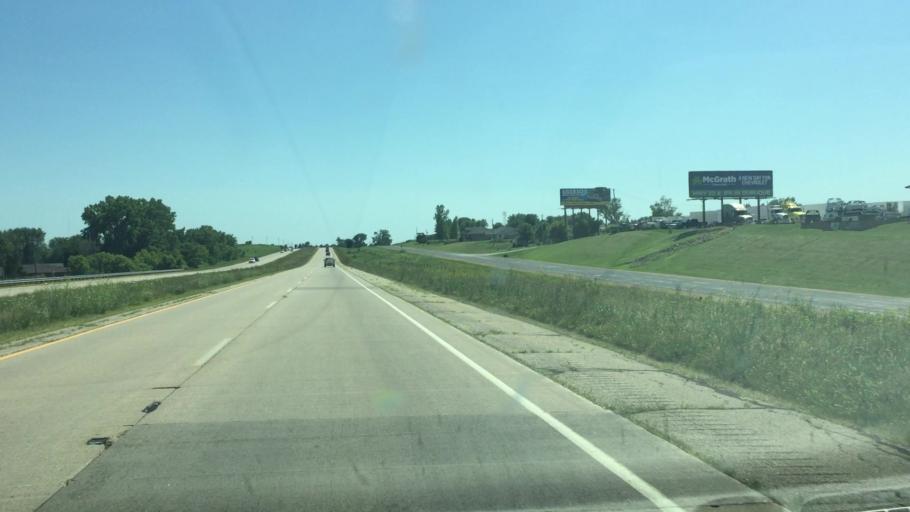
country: US
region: Wisconsin
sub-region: Grant County
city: Dickeyville
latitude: 42.5860
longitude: -90.6043
